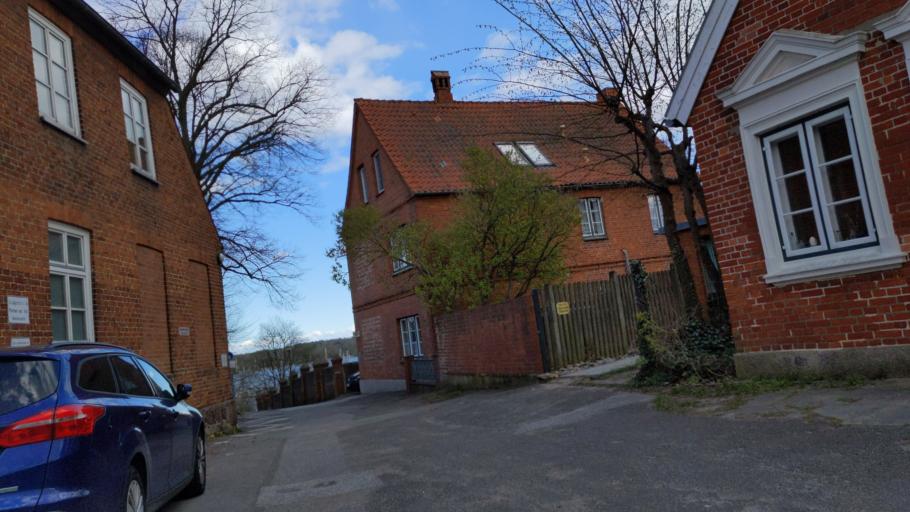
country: DE
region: Mecklenburg-Vorpommern
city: Selmsdorf
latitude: 53.8891
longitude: 10.7997
